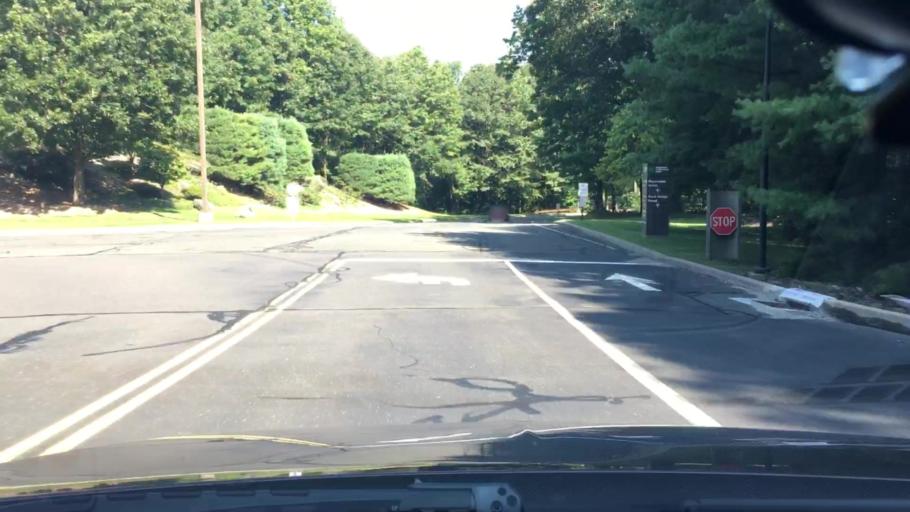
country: US
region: Connecticut
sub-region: Fairfield County
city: Bethel
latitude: 41.4283
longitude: -73.4063
